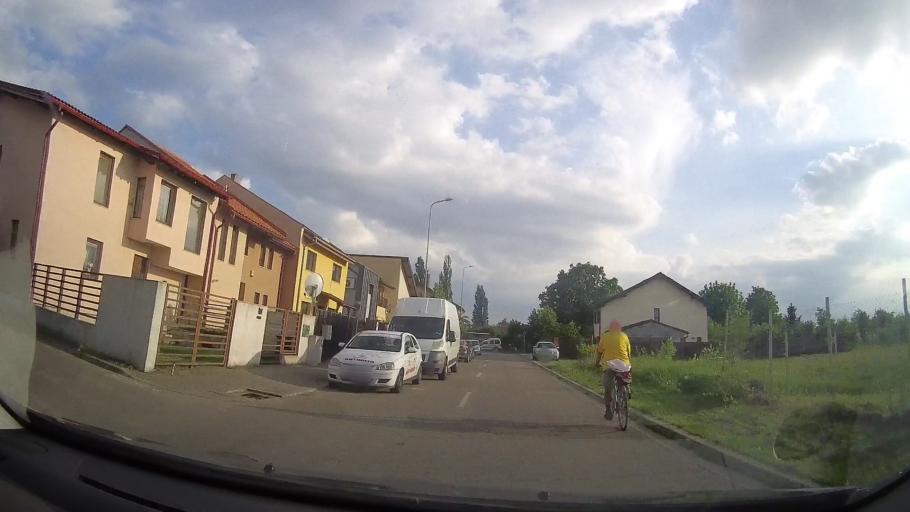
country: RO
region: Timis
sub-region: Comuna Dumbravita
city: Dumbravita
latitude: 45.7829
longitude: 21.2318
